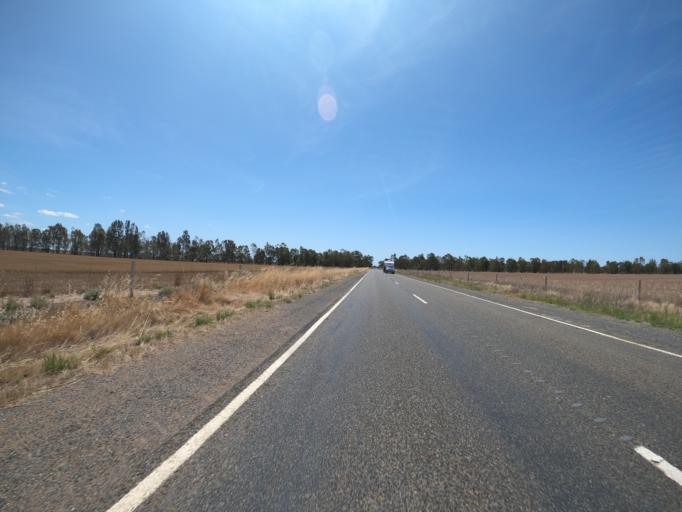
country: AU
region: Victoria
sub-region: Moira
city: Yarrawonga
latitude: -36.1630
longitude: 145.9673
